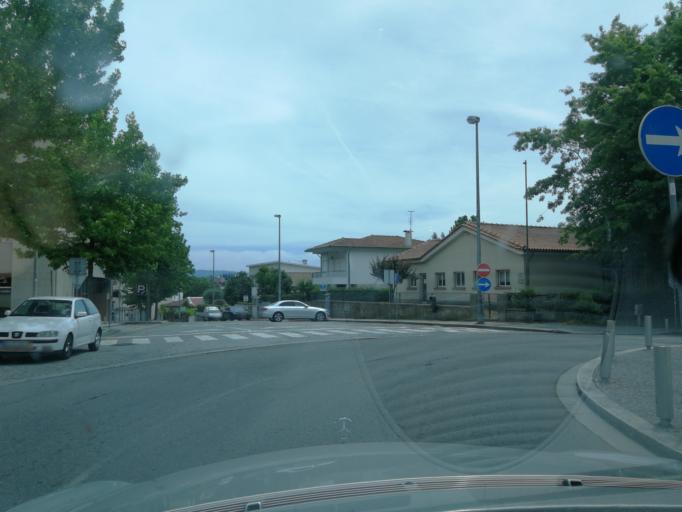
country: PT
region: Braga
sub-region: Vila Nova de Famalicao
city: Vila Nova de Famalicao
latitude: 41.4102
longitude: -8.5223
